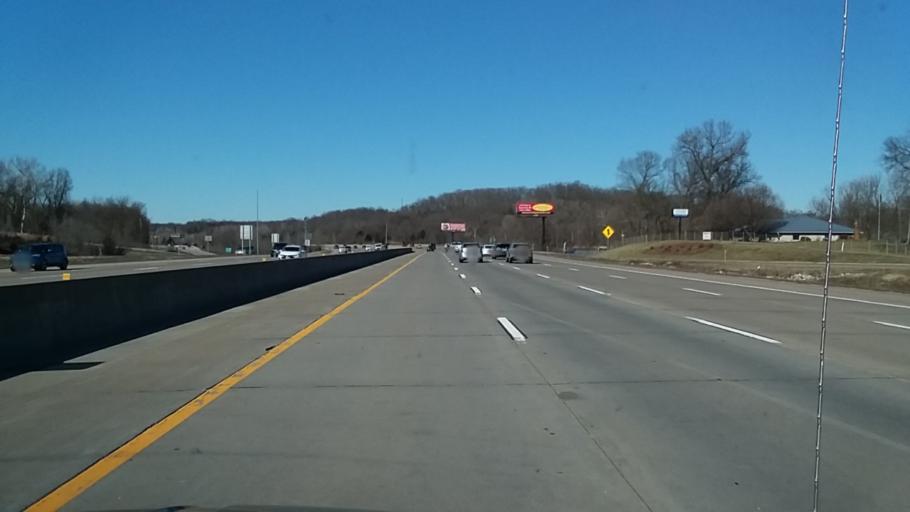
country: US
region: Missouri
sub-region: Jefferson County
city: Imperial
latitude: 38.3707
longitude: -90.3823
